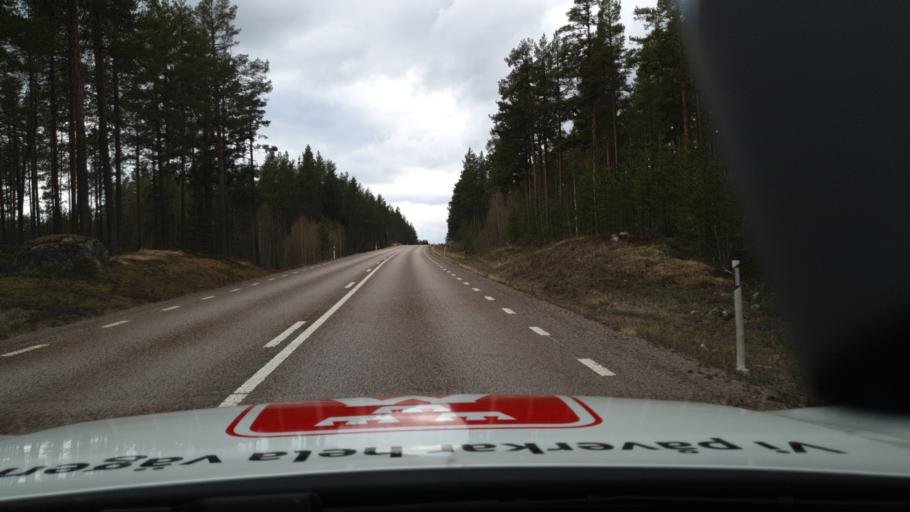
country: SE
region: Jaemtland
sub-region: Braecke Kommun
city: Braecke
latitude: 63.1935
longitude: 15.3064
